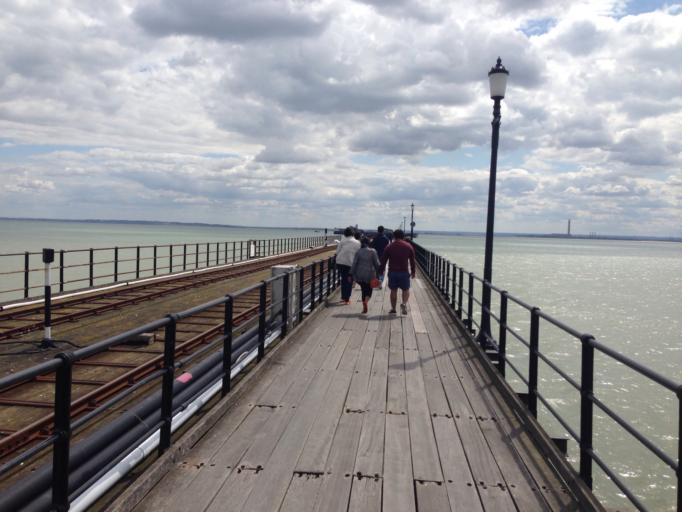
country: GB
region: England
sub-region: Southend-on-Sea
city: Southend-on-Sea
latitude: 51.5248
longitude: 0.7185
